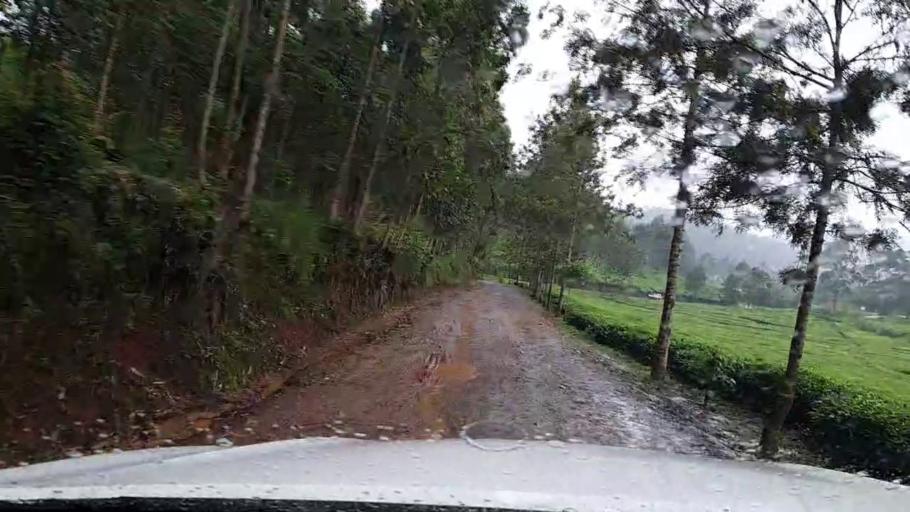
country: RW
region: Western Province
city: Cyangugu
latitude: -2.4497
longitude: 29.0387
